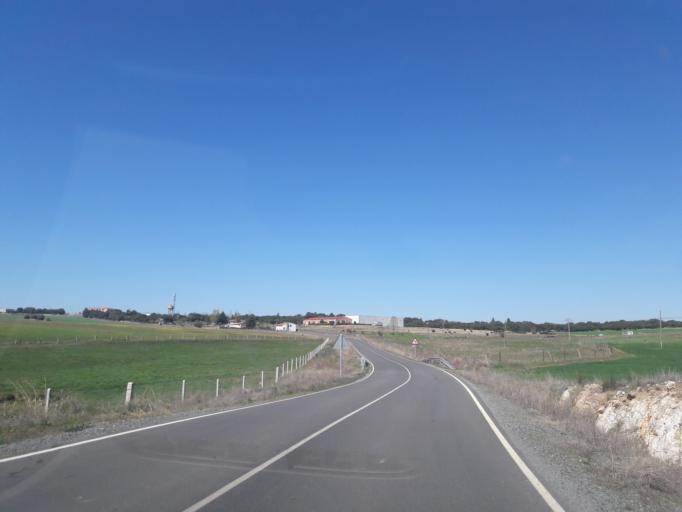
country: ES
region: Castille and Leon
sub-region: Provincia de Salamanca
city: Martinamor
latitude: 40.8094
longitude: -5.6207
